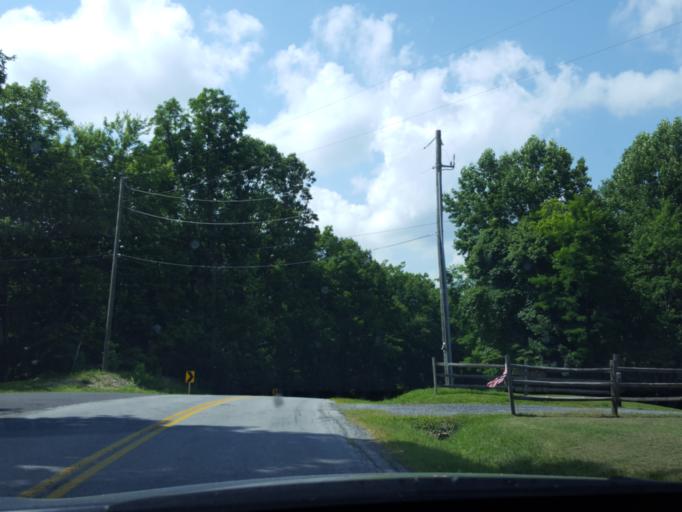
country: US
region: Virginia
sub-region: Nelson County
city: Nellysford
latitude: 37.9071
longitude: -78.9886
